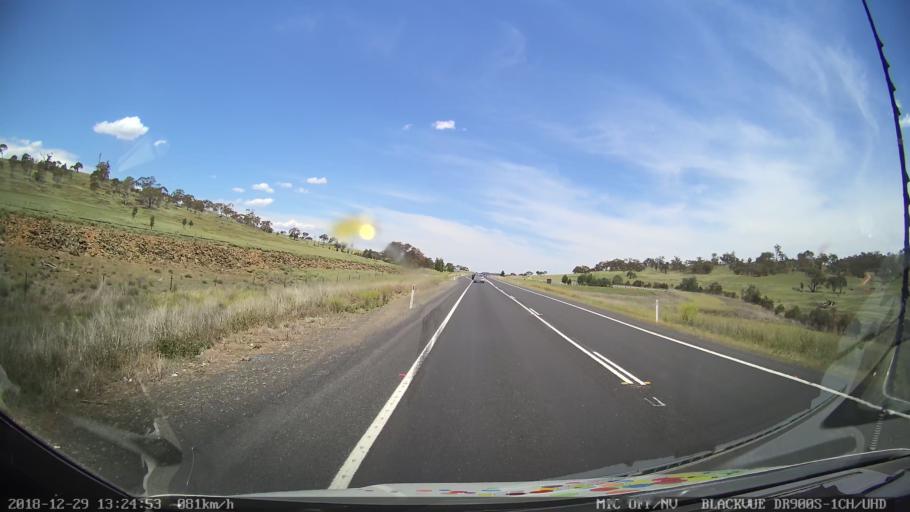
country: AU
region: New South Wales
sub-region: Cooma-Monaro
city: Cooma
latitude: -35.8352
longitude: 149.1622
